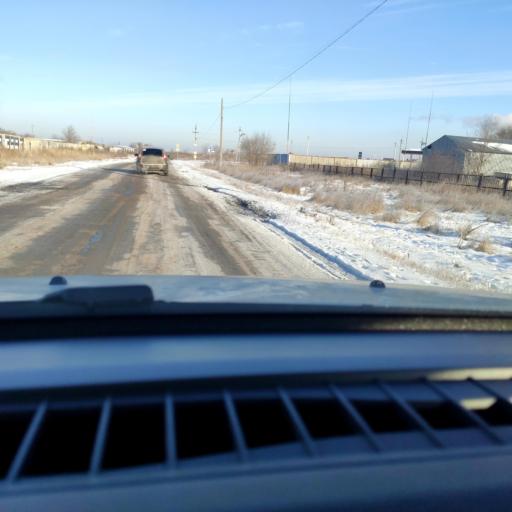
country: RU
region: Samara
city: Podstepki
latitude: 53.5217
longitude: 49.1457
